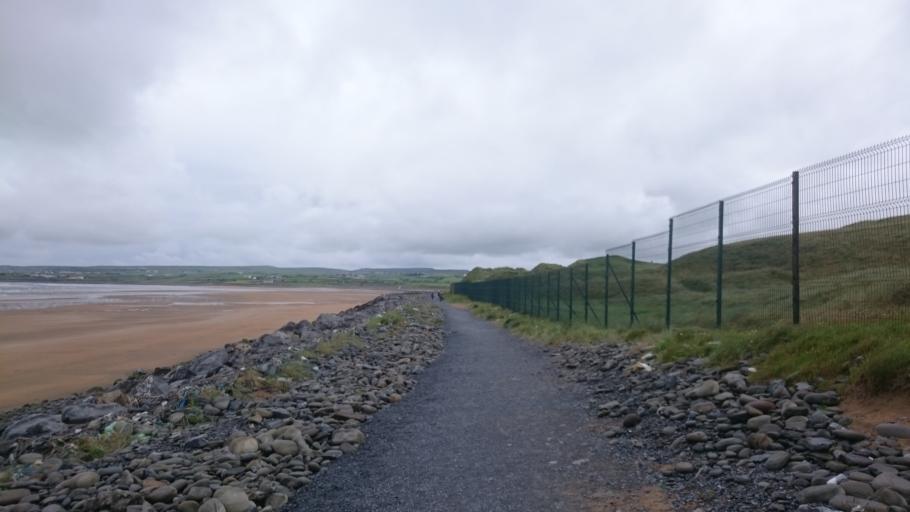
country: IE
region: Munster
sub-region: An Clar
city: Kilrush
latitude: 52.9371
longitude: -9.3533
